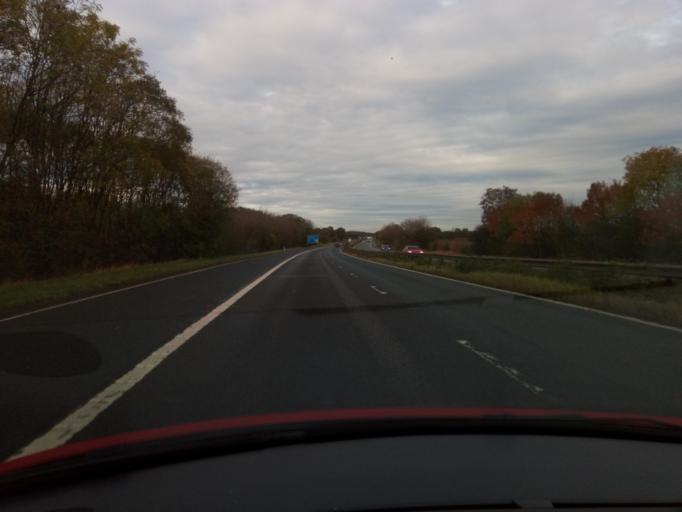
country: GB
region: England
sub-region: Darlington
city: High Coniscliffe
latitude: 54.5435
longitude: -1.6058
